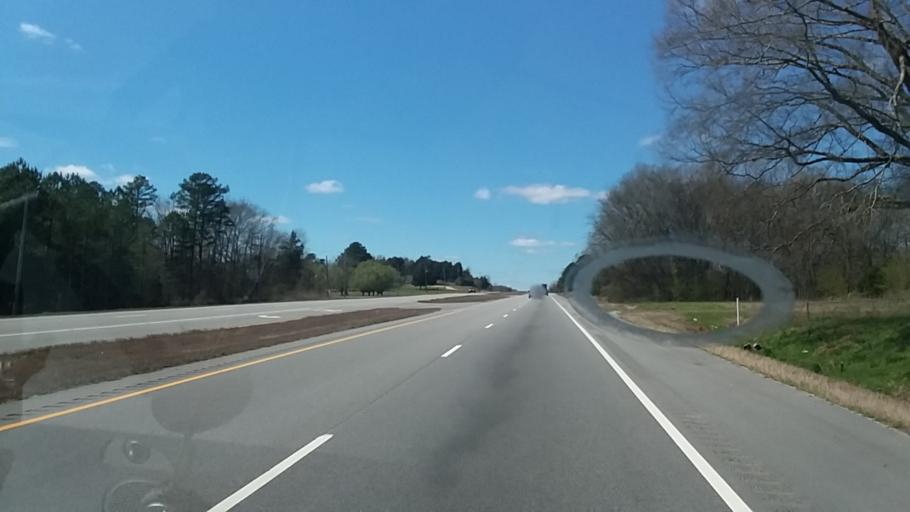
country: US
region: Alabama
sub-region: Colbert County
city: Cherokee
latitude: 34.7310
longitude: -87.8563
